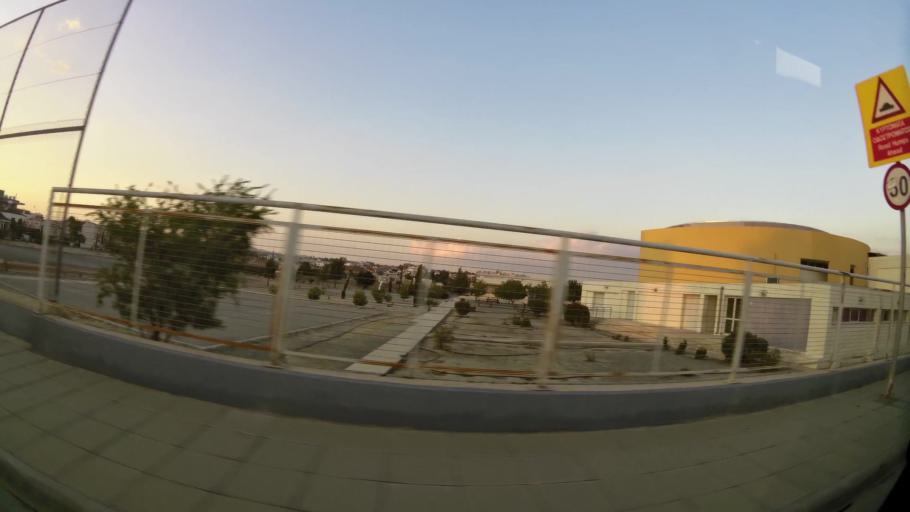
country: CY
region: Larnaka
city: Larnaca
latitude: 34.9159
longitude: 33.5890
